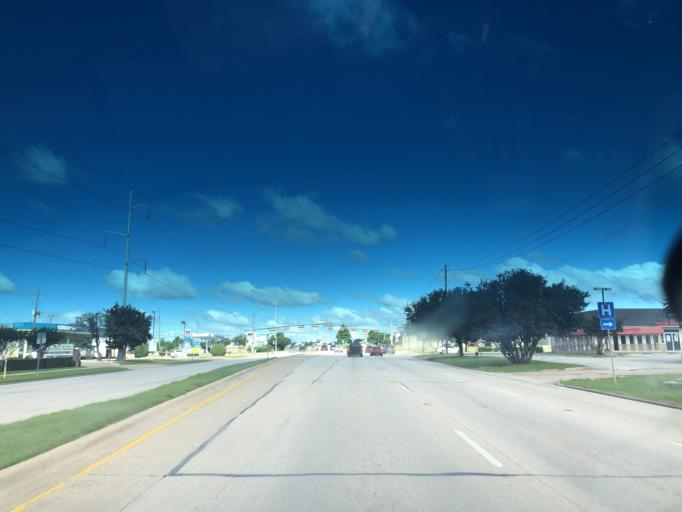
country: US
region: Texas
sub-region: Dallas County
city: Grand Prairie
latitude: 32.7117
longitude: -97.0420
